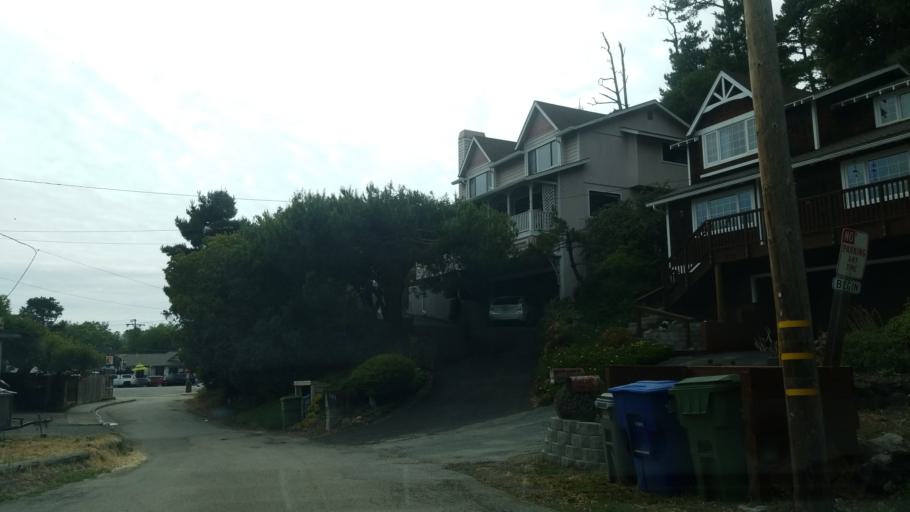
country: US
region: California
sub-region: San Luis Obispo County
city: Cambria
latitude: 35.5683
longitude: -121.1002
